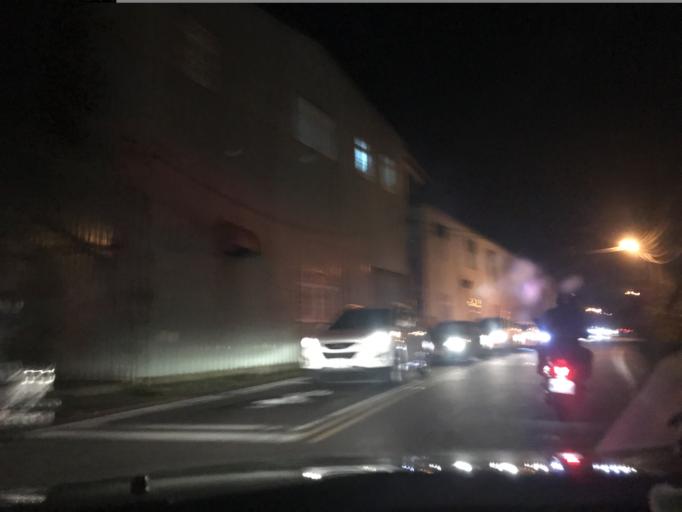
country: TW
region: Taiwan
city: Daxi
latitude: 24.9408
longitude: 121.2425
